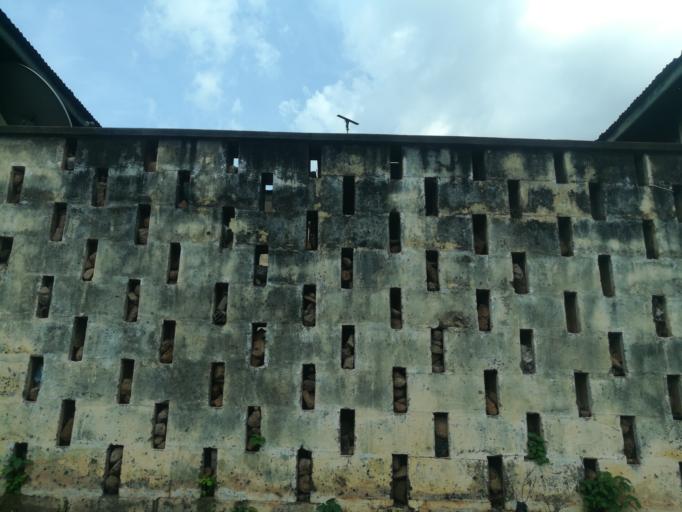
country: NG
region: Oyo
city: Ibadan
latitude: 7.4509
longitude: 3.8988
